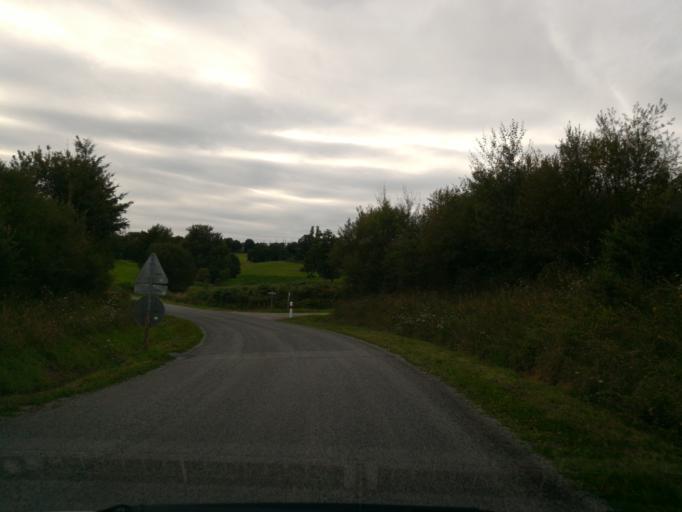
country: FR
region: Limousin
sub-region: Departement de la Haute-Vienne
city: Saint-Junien
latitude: 45.9058
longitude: 0.8637
